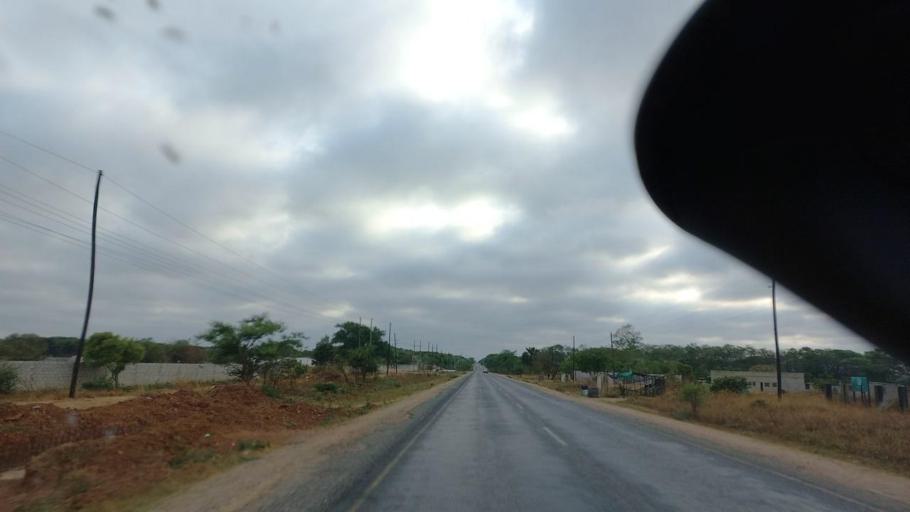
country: ZM
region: Lusaka
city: Chongwe
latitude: -15.3503
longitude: 28.4962
